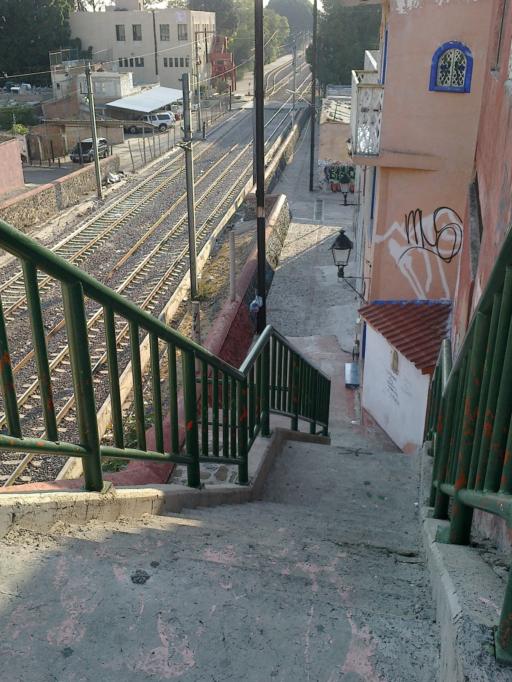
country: MX
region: Queretaro
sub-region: Queretaro
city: Santiago de Queretaro
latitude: 20.6017
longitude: -100.3940
